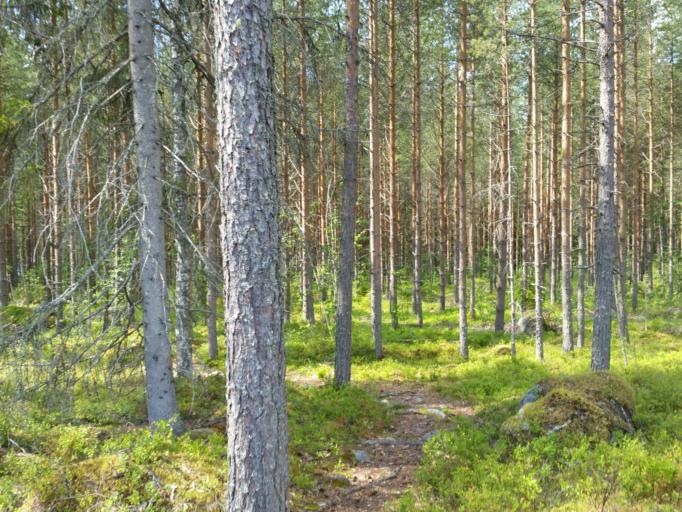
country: FI
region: Northern Savo
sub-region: Ylae-Savo
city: Keitele
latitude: 63.1035
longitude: 26.5324
